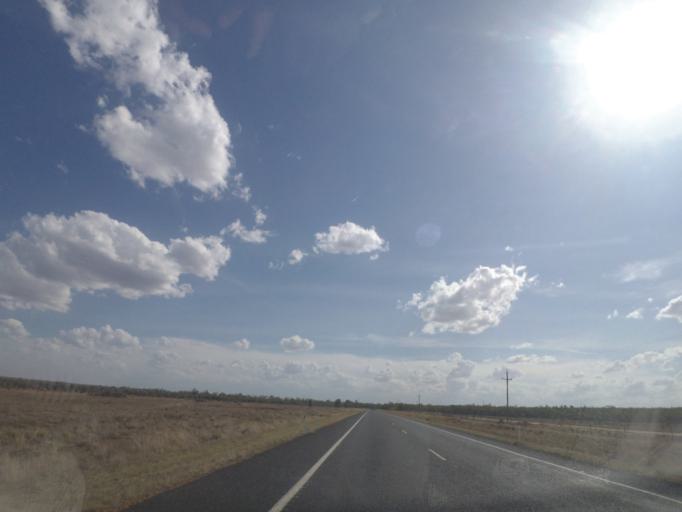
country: AU
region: New South Wales
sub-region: Moree Plains
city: Boggabilla
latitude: -28.5296
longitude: 150.8985
